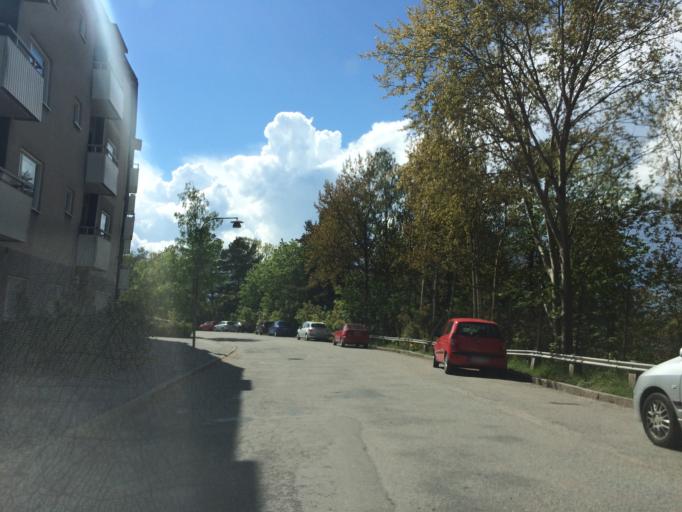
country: SE
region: Stockholm
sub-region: Huddinge Kommun
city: Segeltorp
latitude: 59.2875
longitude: 17.9581
